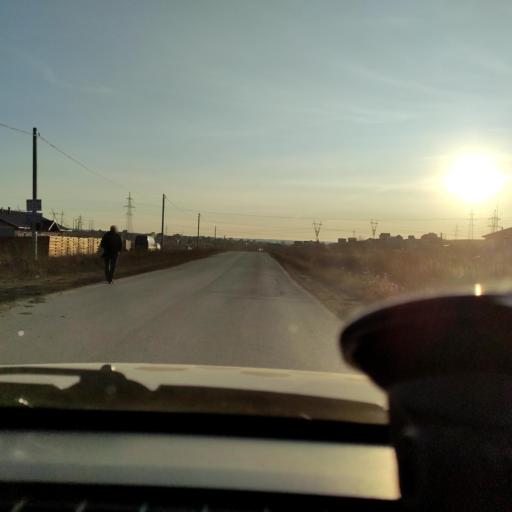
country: RU
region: Perm
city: Ferma
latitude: 57.9537
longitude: 56.3686
